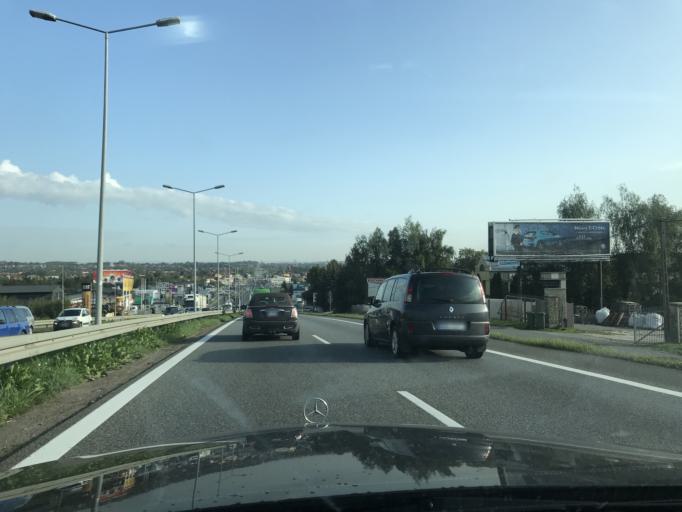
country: PL
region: Lesser Poland Voivodeship
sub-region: Powiat krakowski
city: Libertow
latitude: 49.9743
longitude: 19.9078
